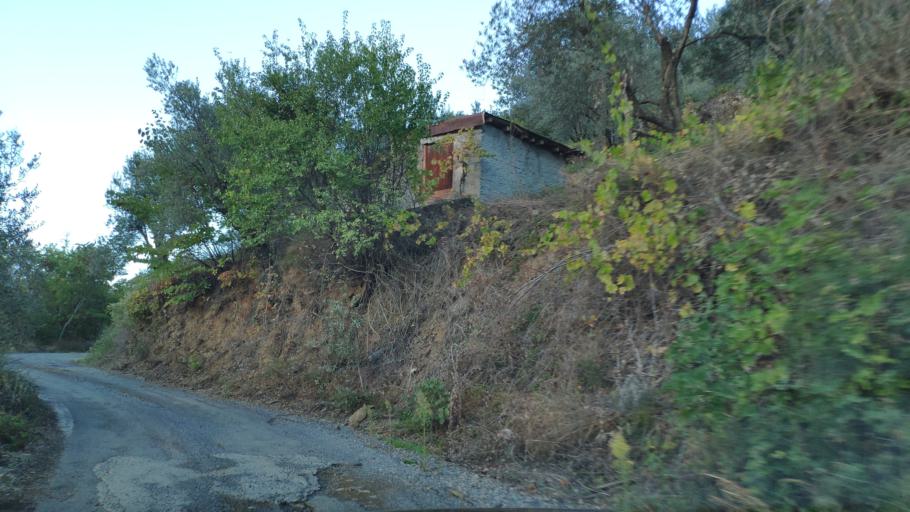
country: GR
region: Peloponnese
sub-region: Nomos Arkadias
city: Dimitsana
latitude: 37.5700
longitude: 22.0468
